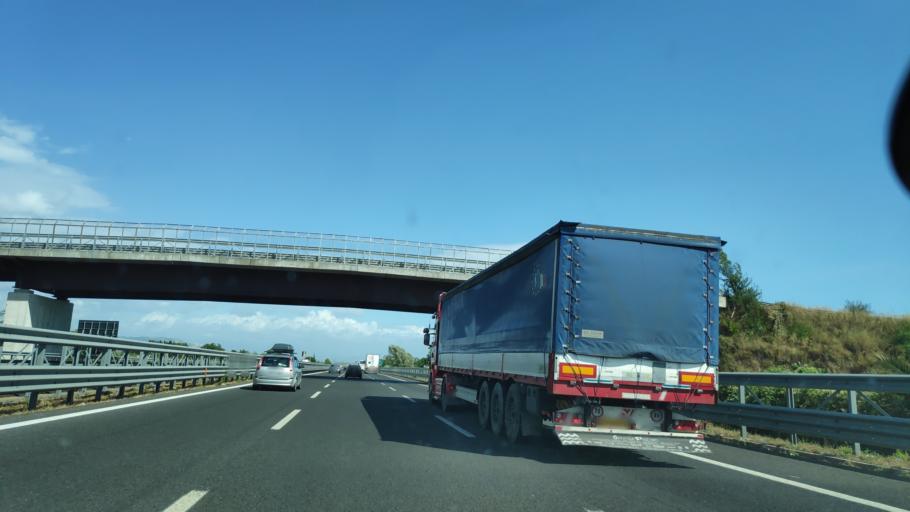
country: IT
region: Campania
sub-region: Provincia di Salerno
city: Pontecagnano
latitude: 40.6462
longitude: 14.8879
